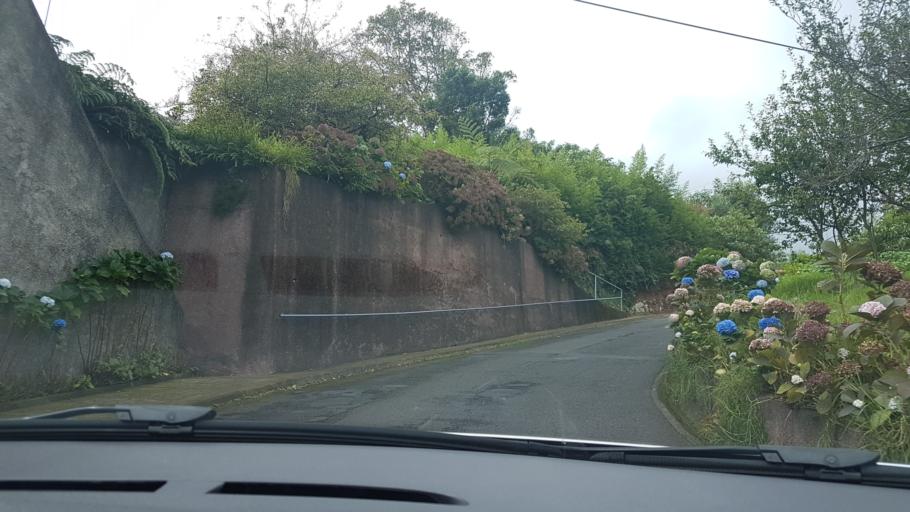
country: PT
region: Madeira
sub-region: Santa Cruz
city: Santa Cruz
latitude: 32.7348
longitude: -16.8199
